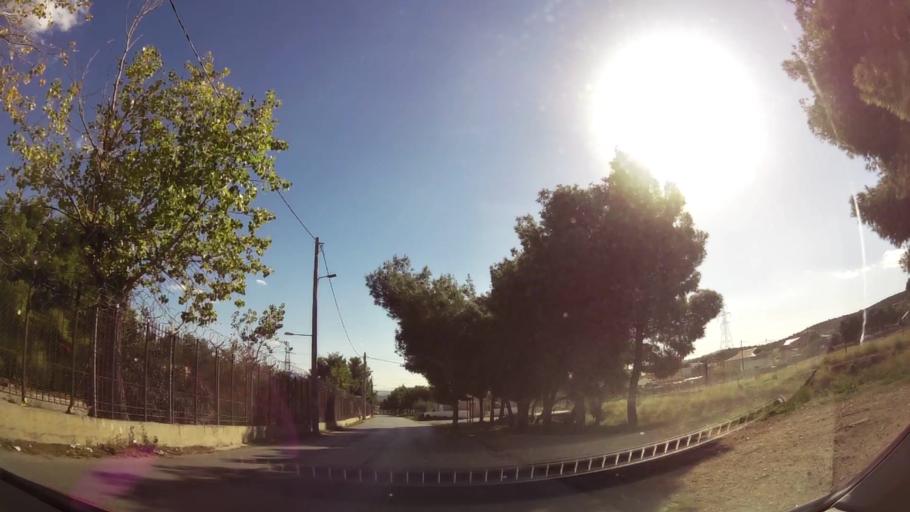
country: GR
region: Attica
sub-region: Nomarchia Anatolikis Attikis
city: Acharnes
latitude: 38.1034
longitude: 23.7237
